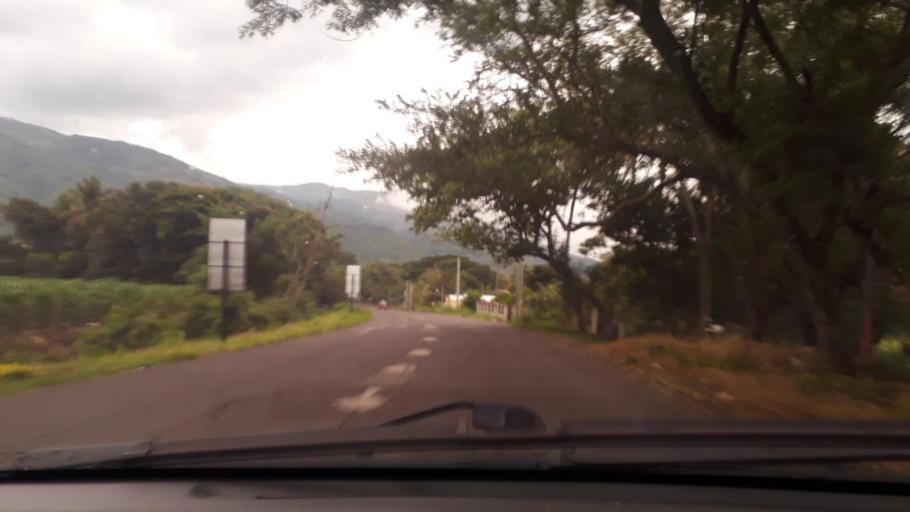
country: GT
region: Jutiapa
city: Jalpatagua
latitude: 14.1249
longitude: -89.9899
